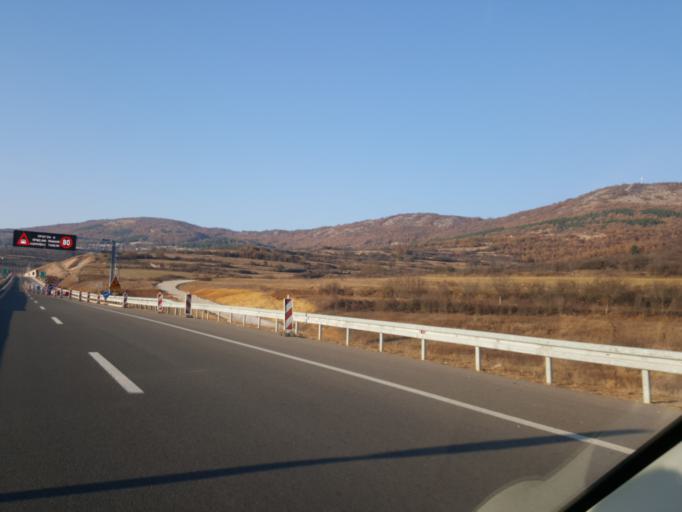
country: RS
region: Central Serbia
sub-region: Pirotski Okrug
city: Dimitrovgrad
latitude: 43.0164
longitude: 22.8005
